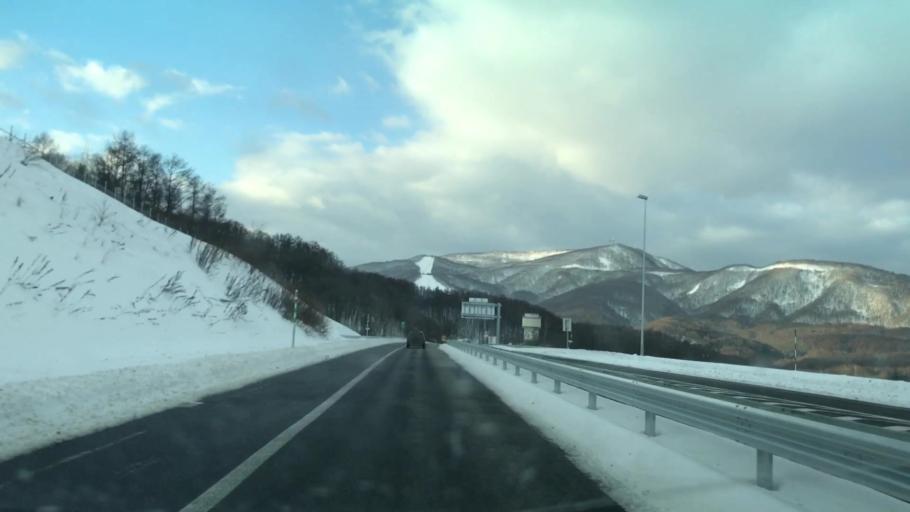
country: JP
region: Hokkaido
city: Otaru
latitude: 43.1627
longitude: 141.0577
